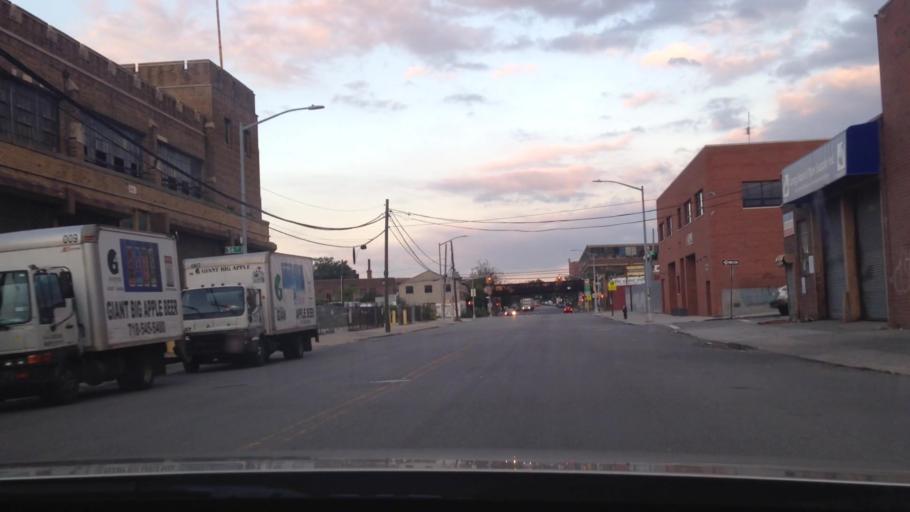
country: US
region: New York
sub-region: Queens County
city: Long Island City
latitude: 40.7189
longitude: -73.9140
